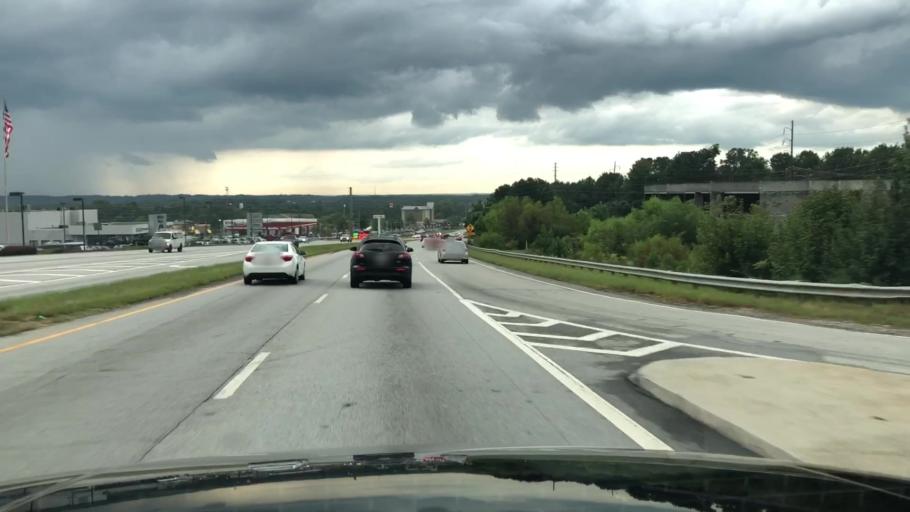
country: US
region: Georgia
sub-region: Cobb County
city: Mableton
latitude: 33.7690
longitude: -84.6007
